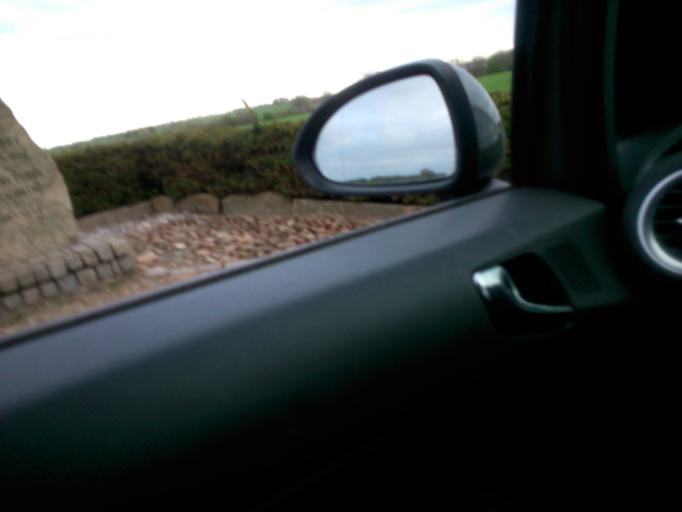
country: DK
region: Central Jutland
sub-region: Ringkobing-Skjern Kommune
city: Videbaek
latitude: 56.0631
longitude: 8.5862
